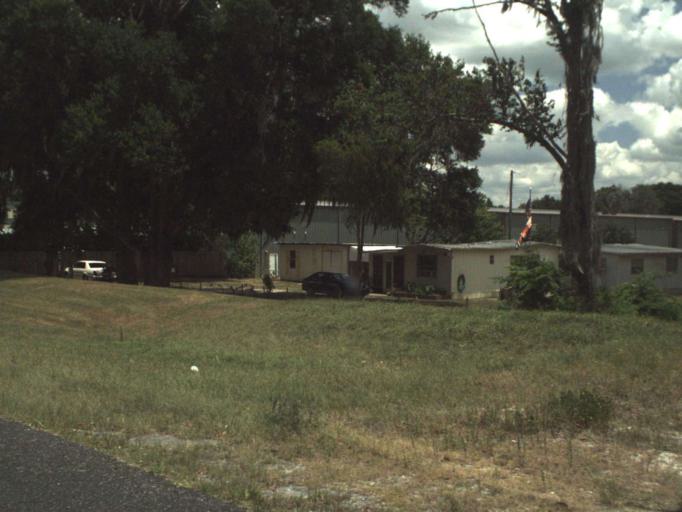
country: US
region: Florida
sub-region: Sumter County
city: Wildwood
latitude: 28.9138
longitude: -82.0369
